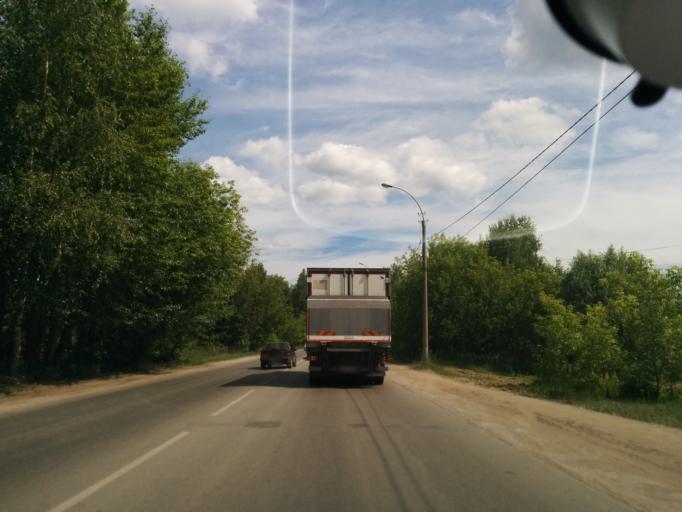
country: RU
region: Perm
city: Overyata
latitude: 58.0148
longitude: 55.9584
